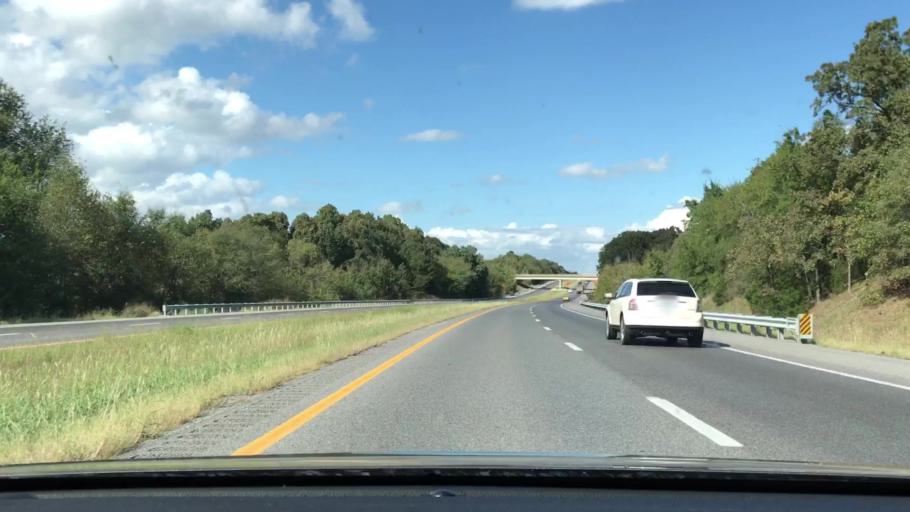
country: US
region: Kentucky
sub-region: Marshall County
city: Calvert City
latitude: 36.9518
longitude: -88.3500
